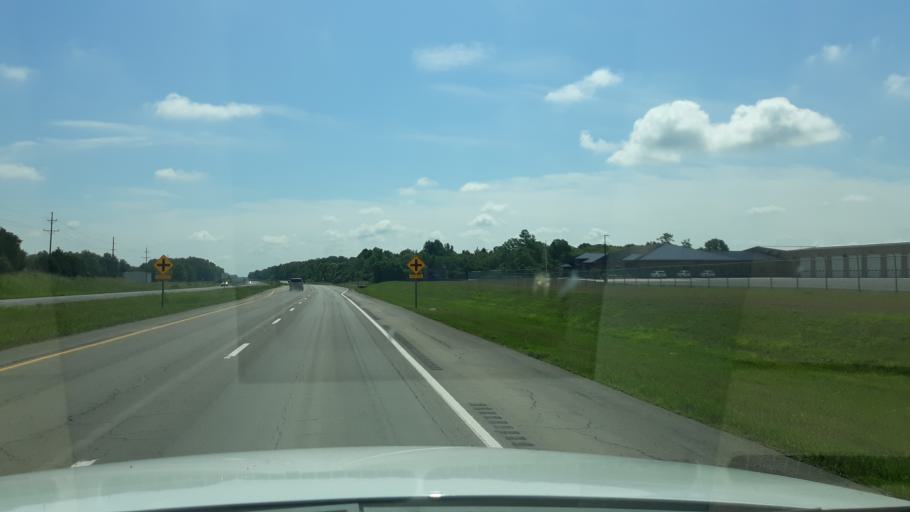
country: US
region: Illinois
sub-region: Saline County
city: Carrier Mills
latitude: 37.7336
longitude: -88.6769
